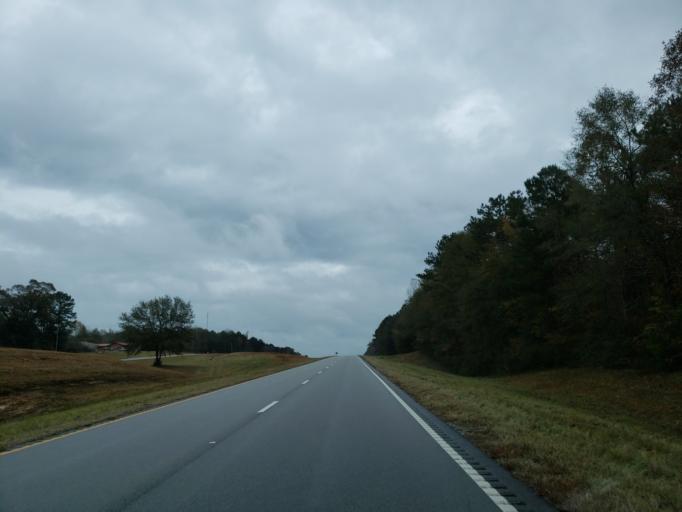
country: US
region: Mississippi
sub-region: Wayne County
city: Waynesboro
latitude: 31.6952
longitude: -88.7519
